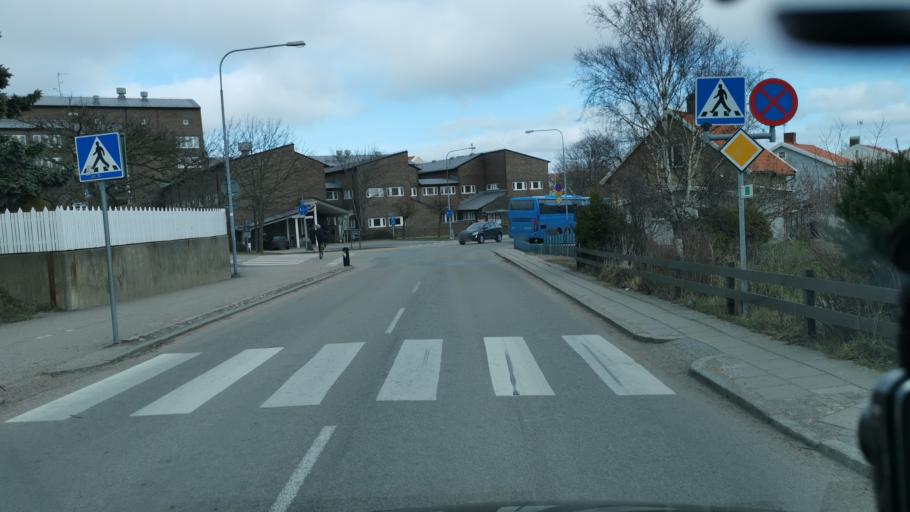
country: SE
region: Vaestra Goetaland
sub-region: Lysekils Kommun
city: Lysekil
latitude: 58.2798
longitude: 11.4391
